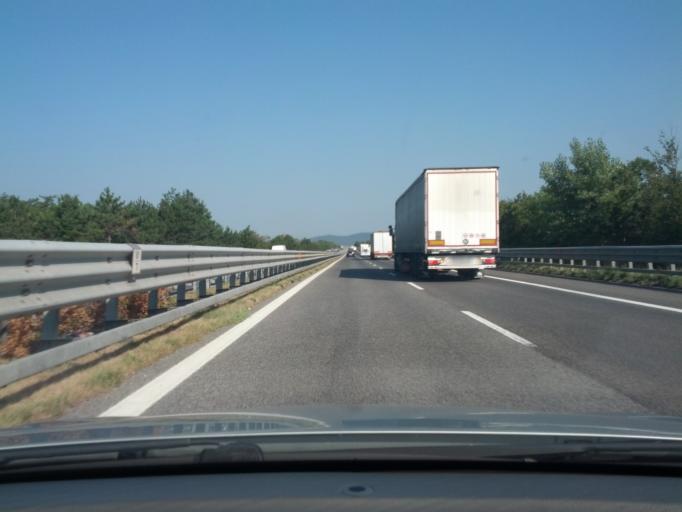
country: IT
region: Friuli Venezia Giulia
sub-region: Provincia di Trieste
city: Santa Croce
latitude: 45.7272
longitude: 13.7157
